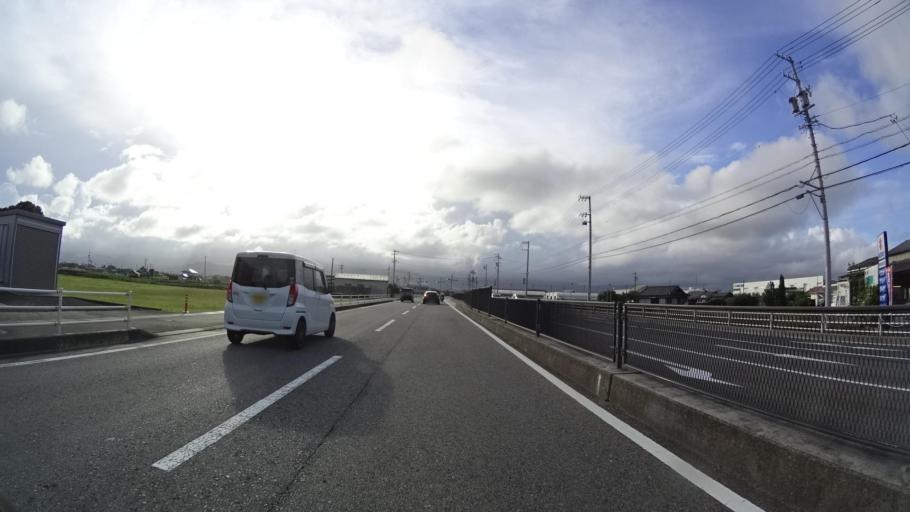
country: JP
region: Mie
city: Kameyama
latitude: 34.9117
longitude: 136.4980
